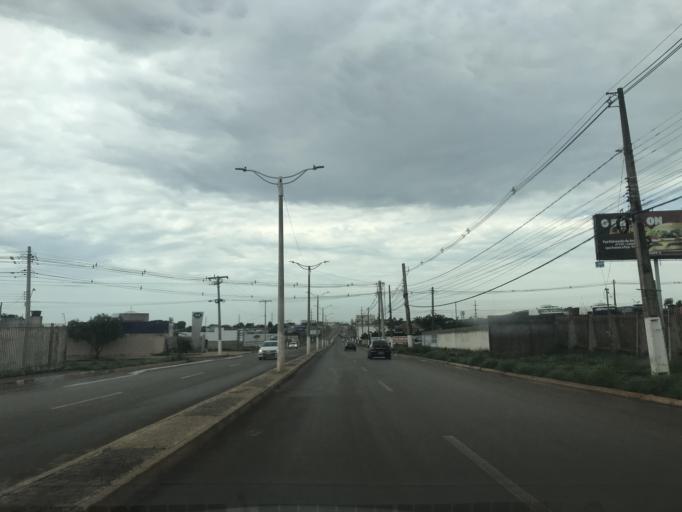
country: BR
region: Goias
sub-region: Luziania
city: Luziania
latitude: -16.2286
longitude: -47.9389
